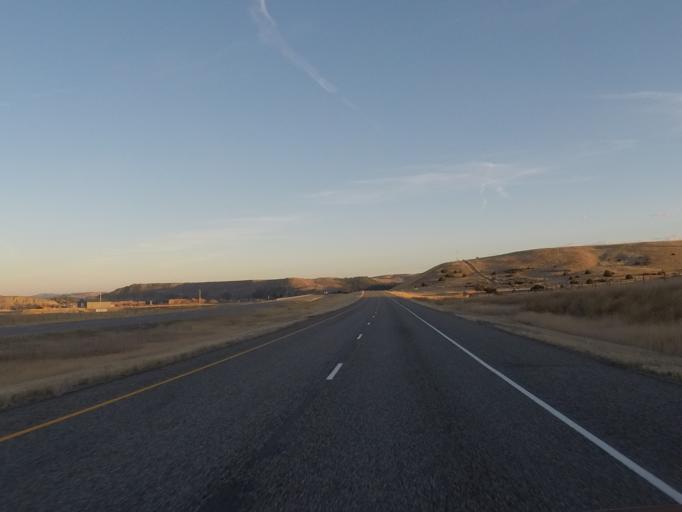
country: US
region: Montana
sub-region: Sweet Grass County
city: Big Timber
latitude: 45.7471
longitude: -109.7734
